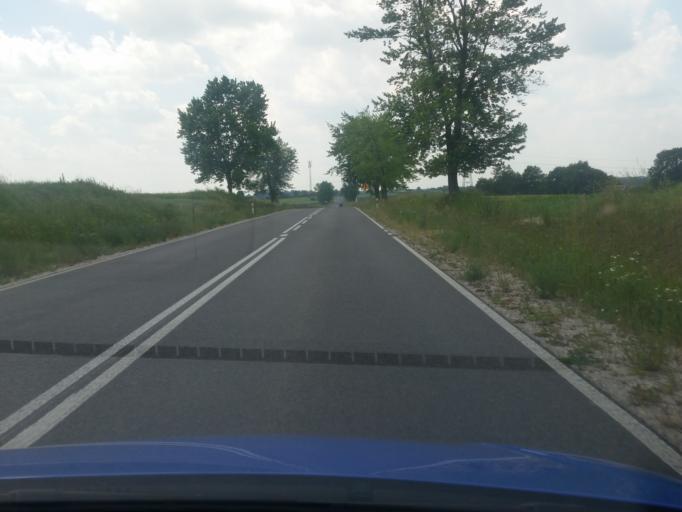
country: PL
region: Swietokrzyskie
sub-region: Powiat pinczowski
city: Zlota
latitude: 50.3290
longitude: 20.5771
